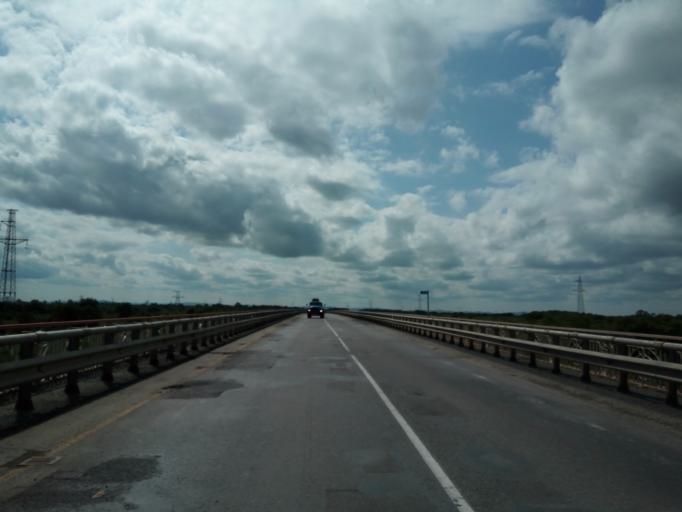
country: RU
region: Primorskiy
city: Dal'nerechensk
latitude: 45.9617
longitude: 133.7836
